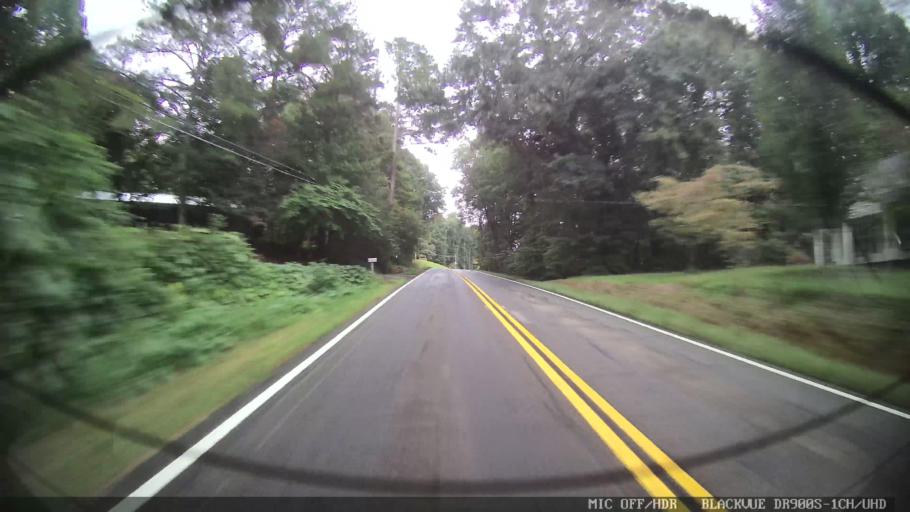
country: US
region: Georgia
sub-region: Gilmer County
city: Ellijay
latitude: 34.7341
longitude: -84.5134
